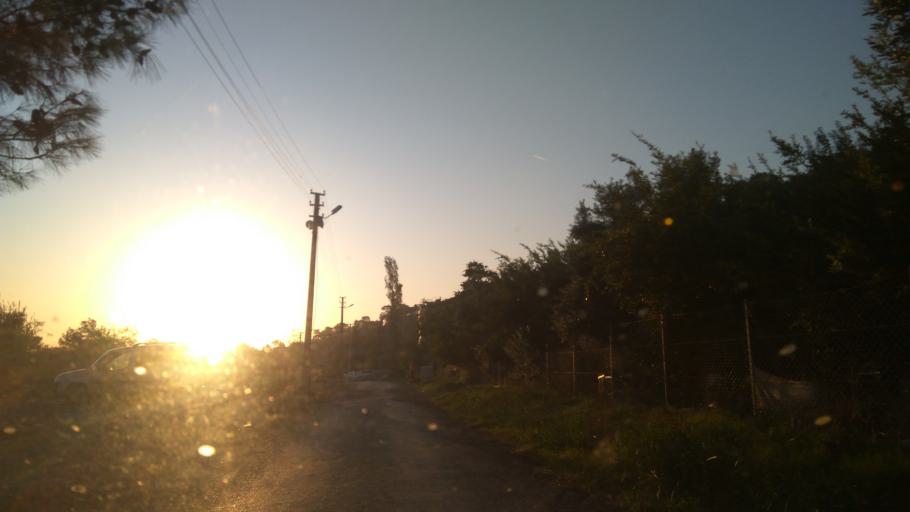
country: TR
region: Antalya
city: Kemer
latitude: 36.5783
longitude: 30.5408
